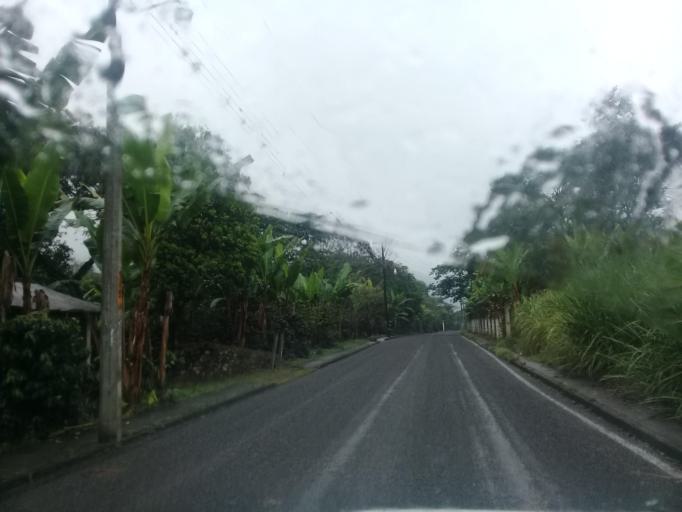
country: MX
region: Veracruz
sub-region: Amatlan de los Reyes
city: Centro de Readaptacion Social
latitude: 18.8002
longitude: -96.9442
